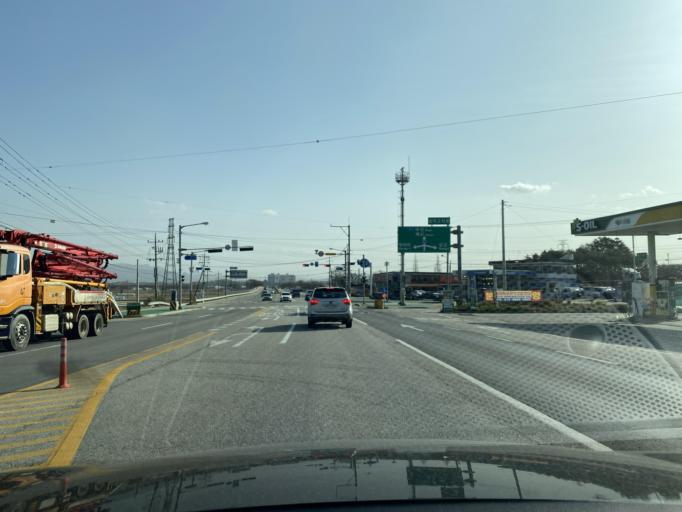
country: KR
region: Chungcheongnam-do
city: Yesan
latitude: 36.6877
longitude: 126.7582
